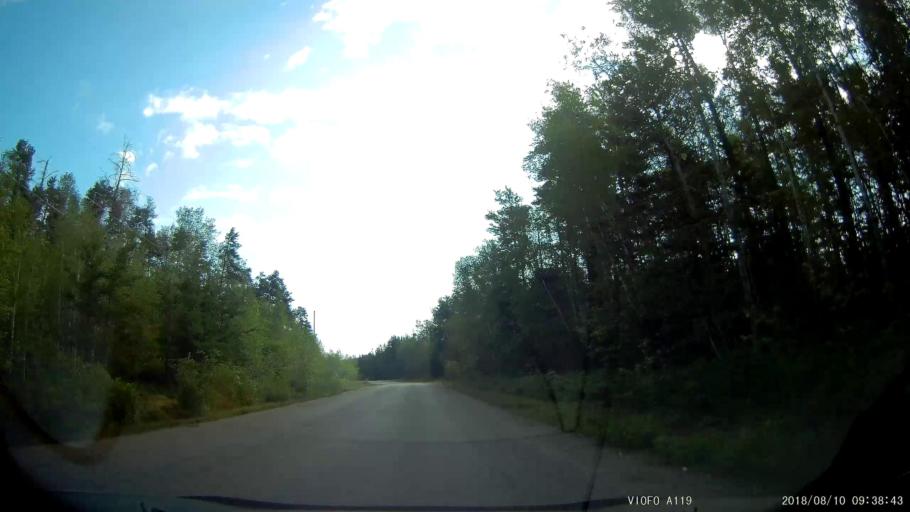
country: CA
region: Ontario
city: Rayside-Balfour
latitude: 46.6198
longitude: -81.4603
